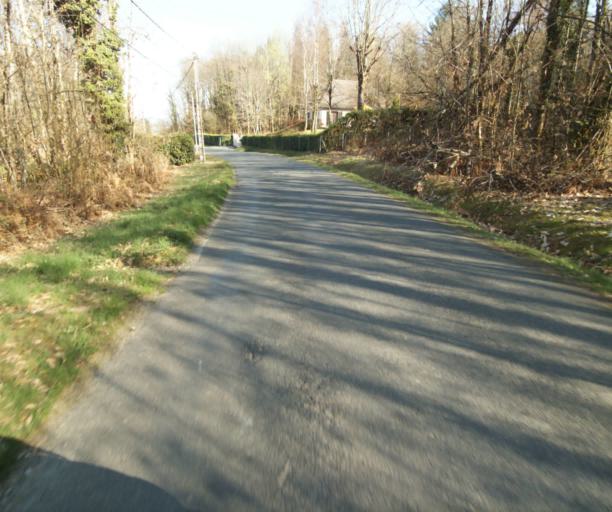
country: FR
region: Limousin
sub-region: Departement de la Correze
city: Saint-Mexant
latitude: 45.2949
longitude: 1.6962
